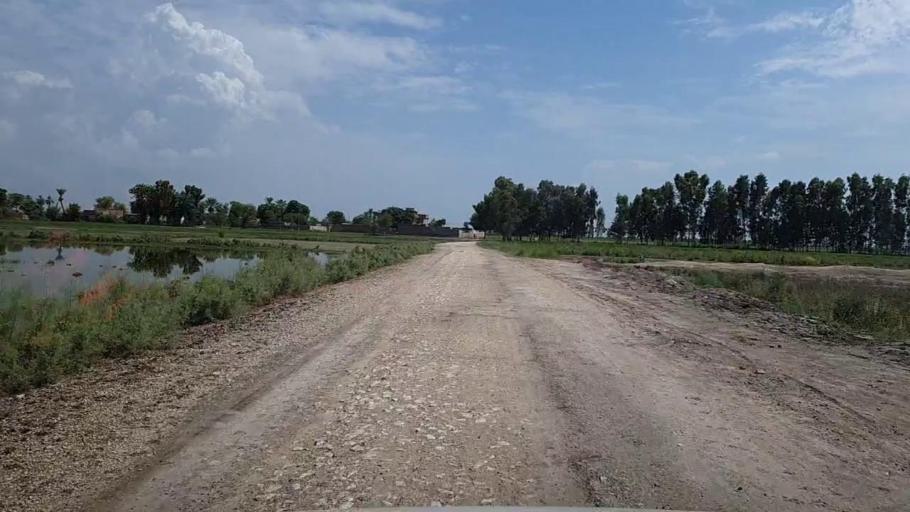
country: PK
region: Sindh
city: Bhiria
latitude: 26.9486
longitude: 68.2431
